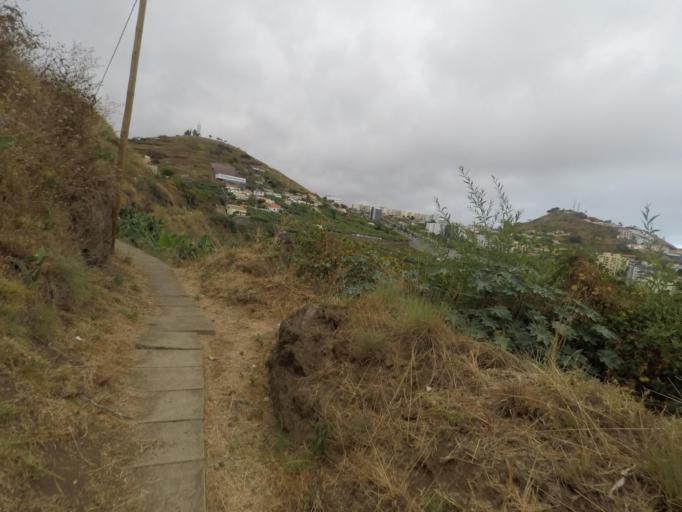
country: PT
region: Madeira
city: Camara de Lobos
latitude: 32.6454
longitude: -16.9498
